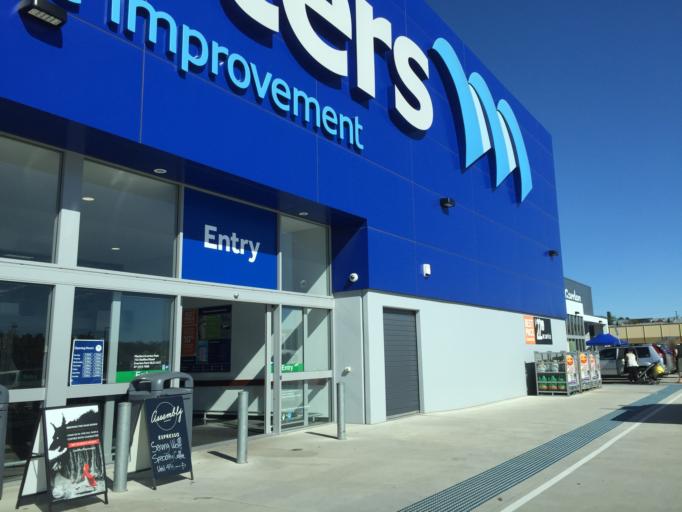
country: AU
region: Queensland
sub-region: Brisbane
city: Everton Park
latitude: -27.4081
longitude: 152.9936
